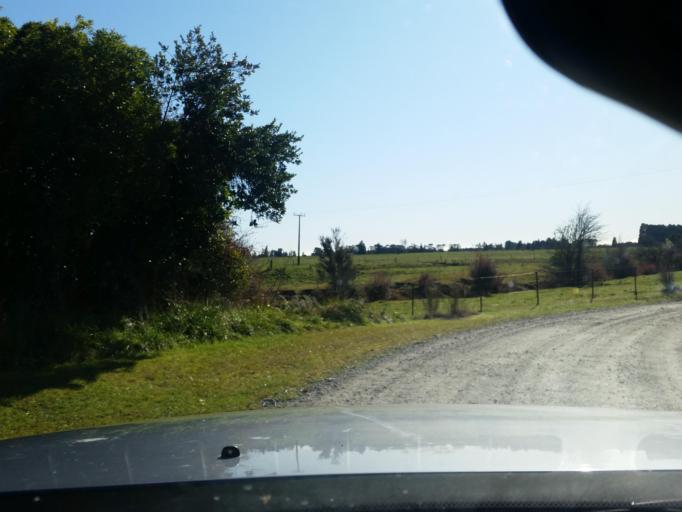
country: NZ
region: Tasman
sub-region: Tasman District
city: Takaka
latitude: -40.8102
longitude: 172.7573
